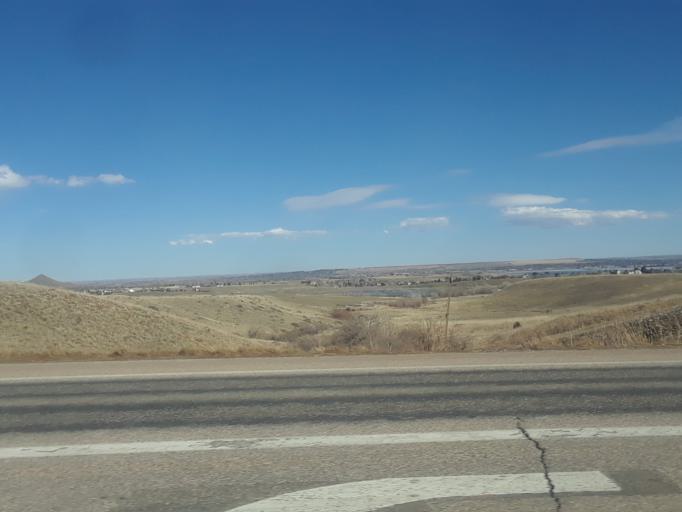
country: US
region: Colorado
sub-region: Boulder County
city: Boulder
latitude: 40.0996
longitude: -105.2820
